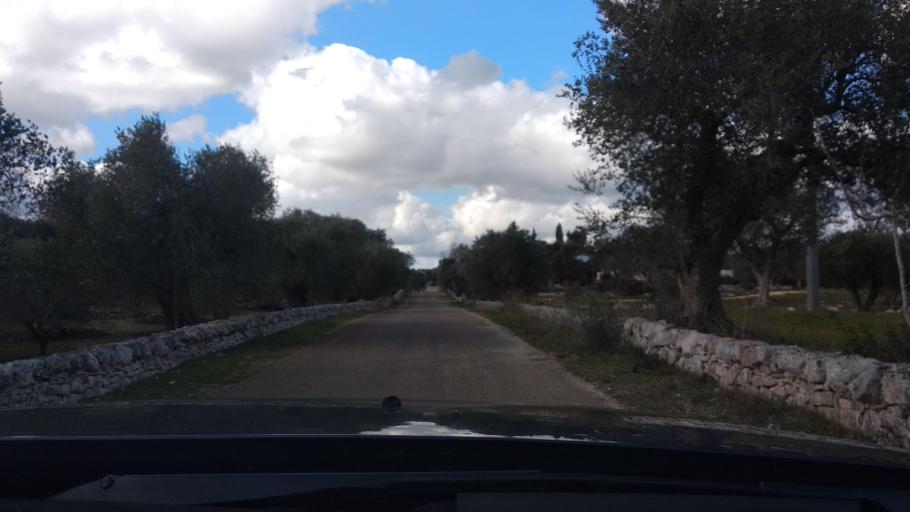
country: IT
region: Apulia
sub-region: Provincia di Brindisi
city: Casalini
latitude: 40.6995
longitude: 17.4657
